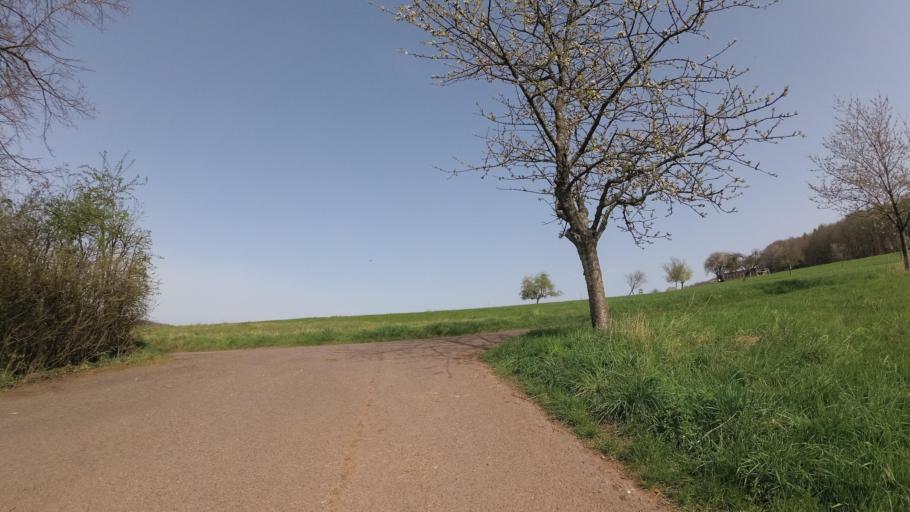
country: DE
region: Saarland
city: Illingen
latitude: 49.3998
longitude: 7.0398
